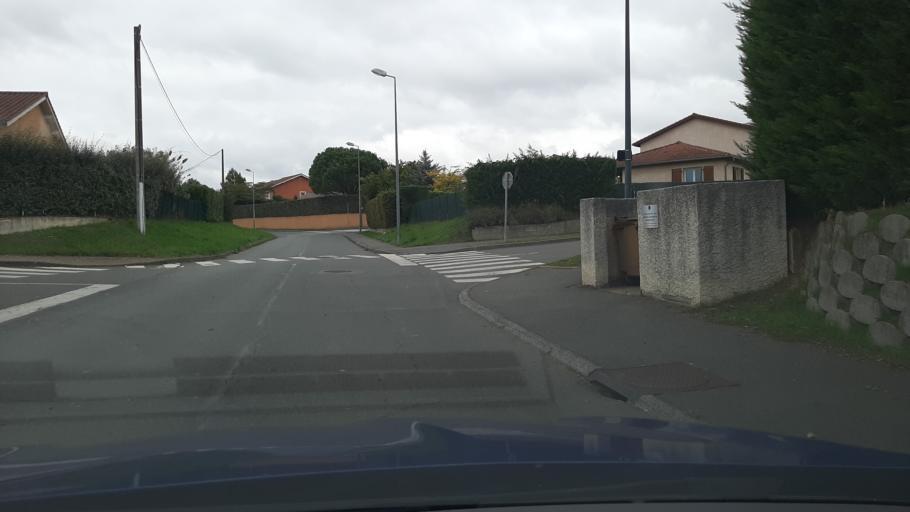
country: FR
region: Rhone-Alpes
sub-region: Departement du Rhone
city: Belleville
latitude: 46.1096
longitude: 4.7211
